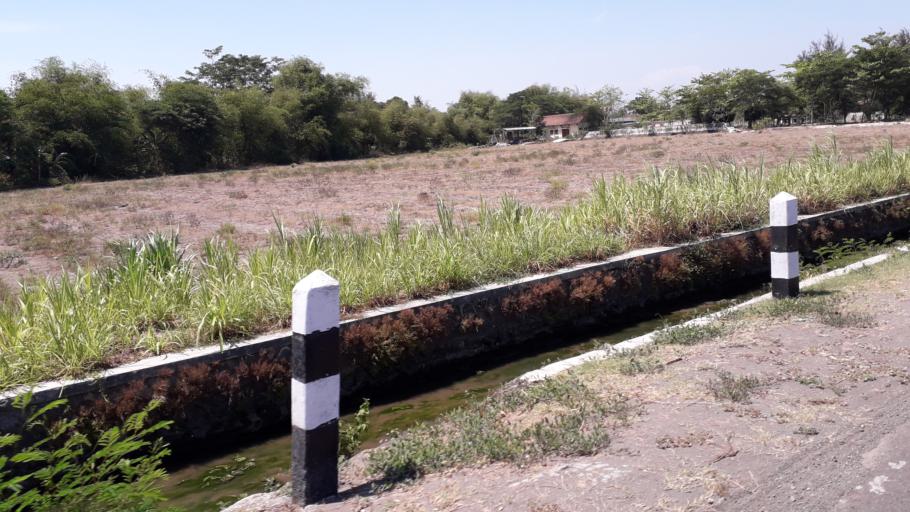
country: ID
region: Daerah Istimewa Yogyakarta
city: Pundong
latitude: -7.9440
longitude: 110.3314
